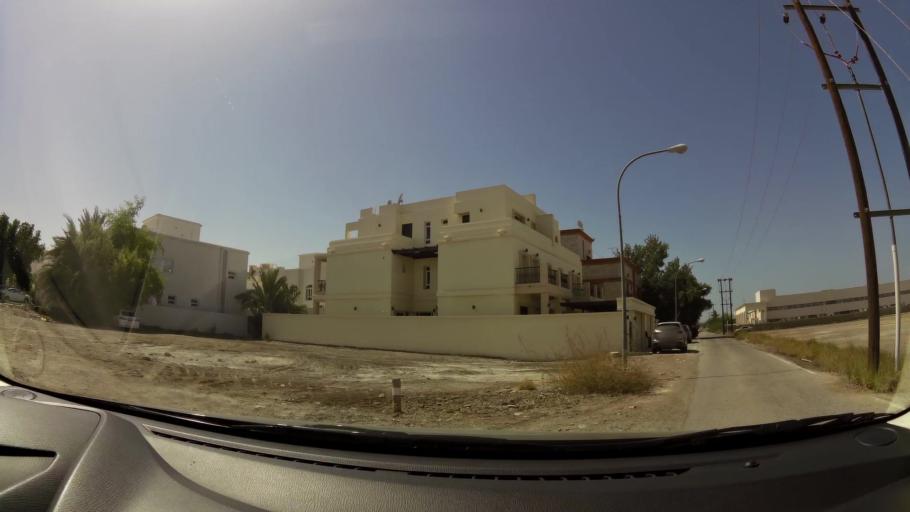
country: OM
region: Muhafazat Masqat
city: Bawshar
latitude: 23.5989
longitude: 58.3485
